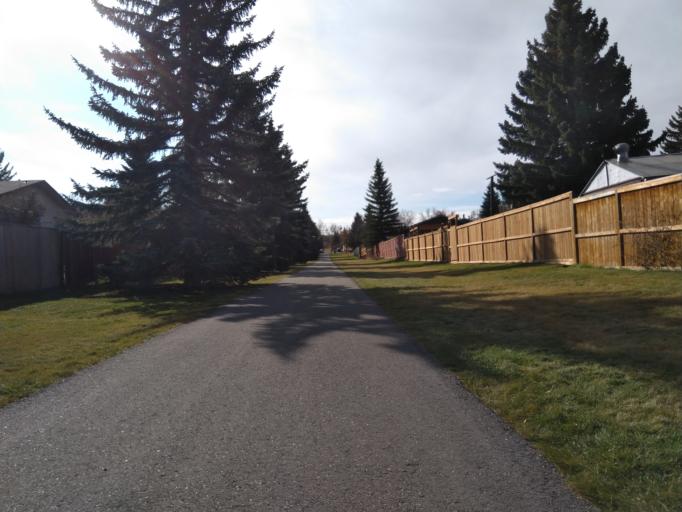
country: CA
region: Alberta
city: Calgary
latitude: 51.1290
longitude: -114.0843
